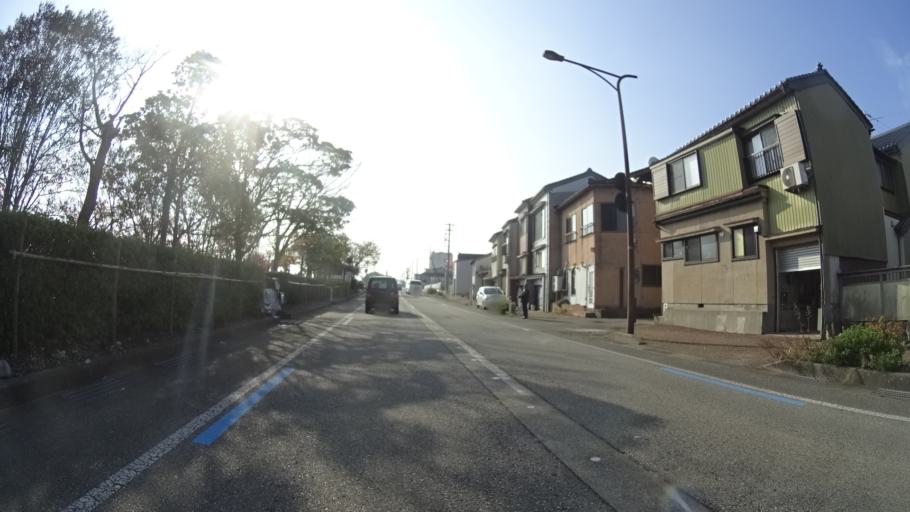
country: JP
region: Toyama
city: Himi
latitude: 36.8563
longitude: 136.9896
